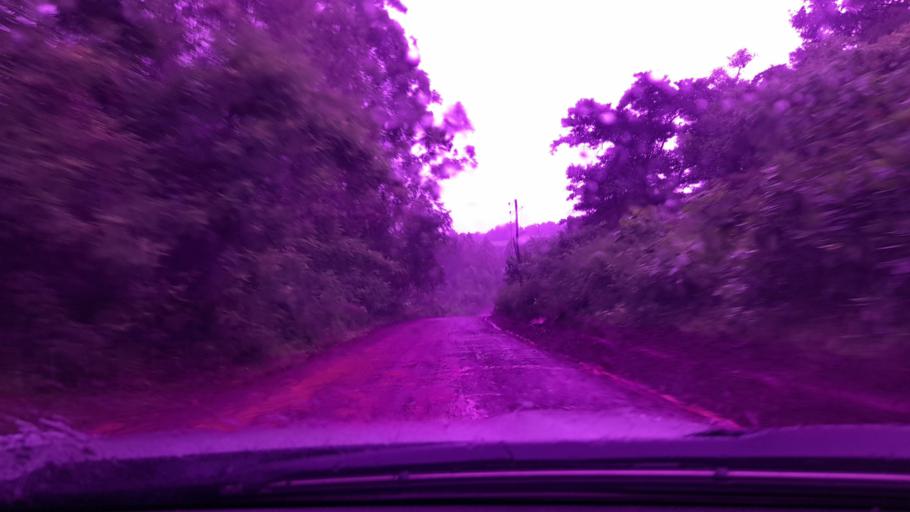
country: ET
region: Oromiya
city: Metu
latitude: 8.3297
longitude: 35.6038
